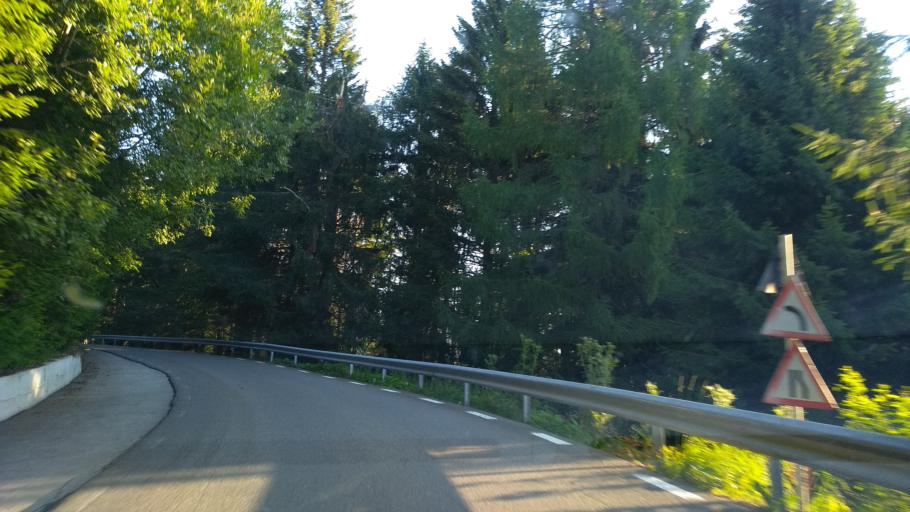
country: RO
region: Prahova
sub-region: Oras Sinaia
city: Sinaia
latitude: 45.3198
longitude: 25.4881
